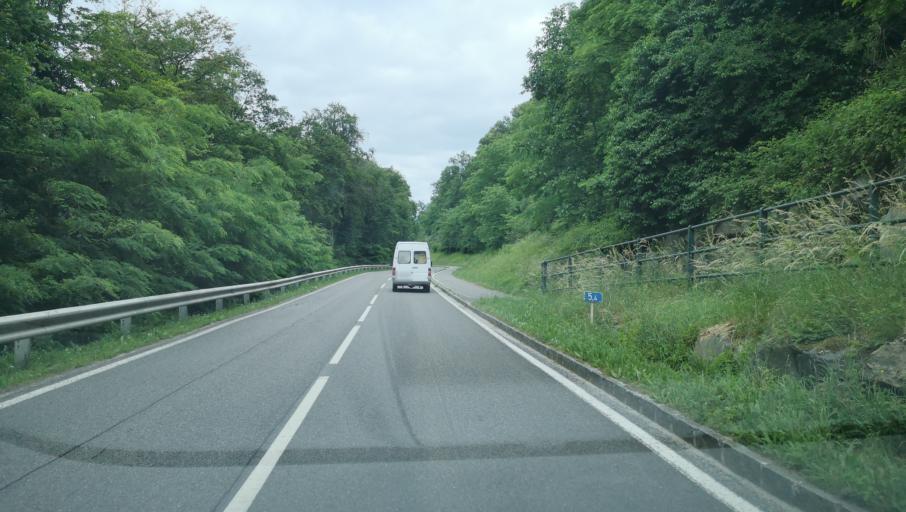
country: AT
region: Lower Austria
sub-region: Politischer Bezirk Krems
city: Aggsbach
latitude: 48.2643
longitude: 15.3791
